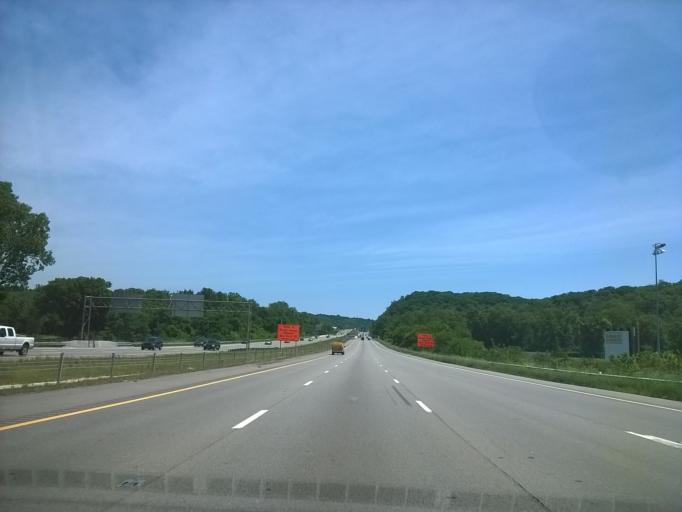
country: US
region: Ohio
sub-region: Hamilton County
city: Miamitown
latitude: 39.2075
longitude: -84.7034
